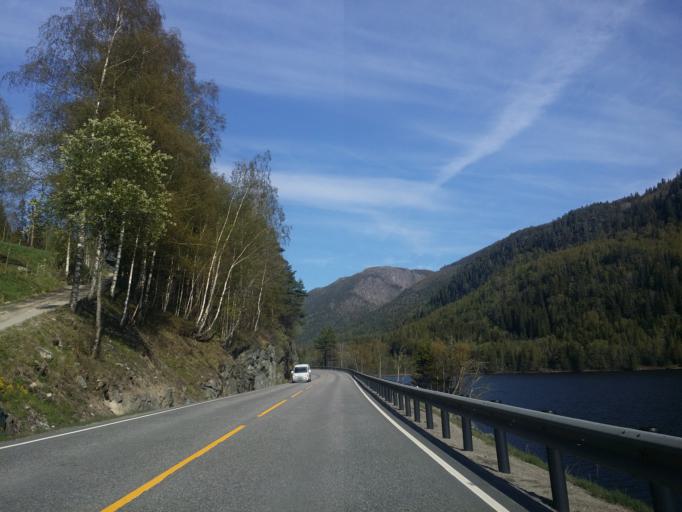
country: NO
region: Telemark
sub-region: Seljord
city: Seljord
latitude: 59.6057
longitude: 8.7342
